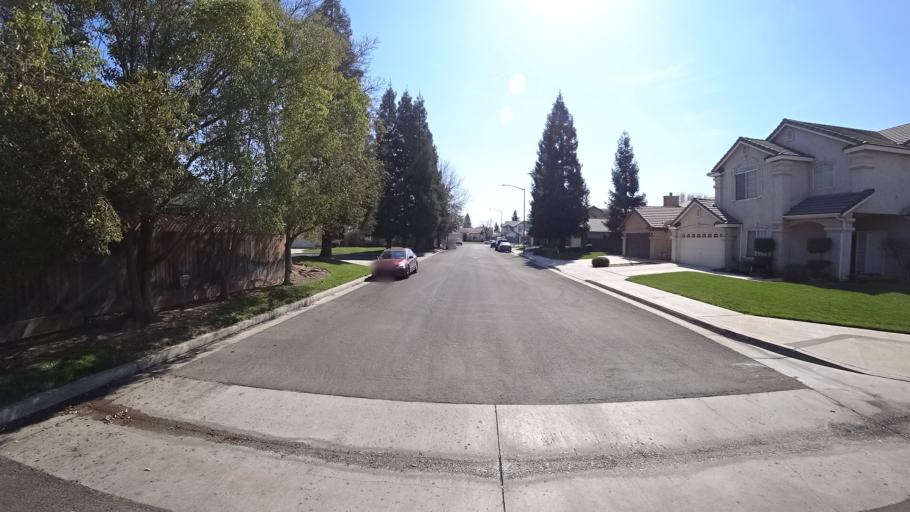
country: US
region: California
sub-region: Fresno County
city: Clovis
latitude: 36.8827
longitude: -119.7428
